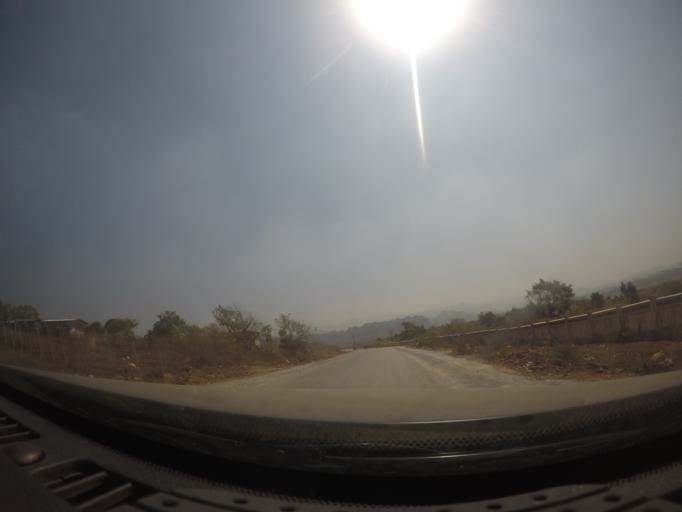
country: MM
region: Shan
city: Taunggyi
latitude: 20.8172
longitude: 97.2137
